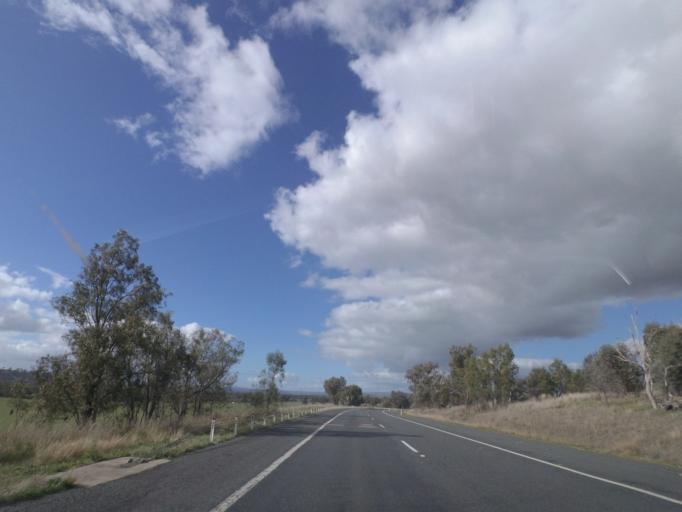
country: AU
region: New South Wales
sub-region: Greater Hume Shire
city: Holbrook
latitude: -35.6713
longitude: 147.4019
